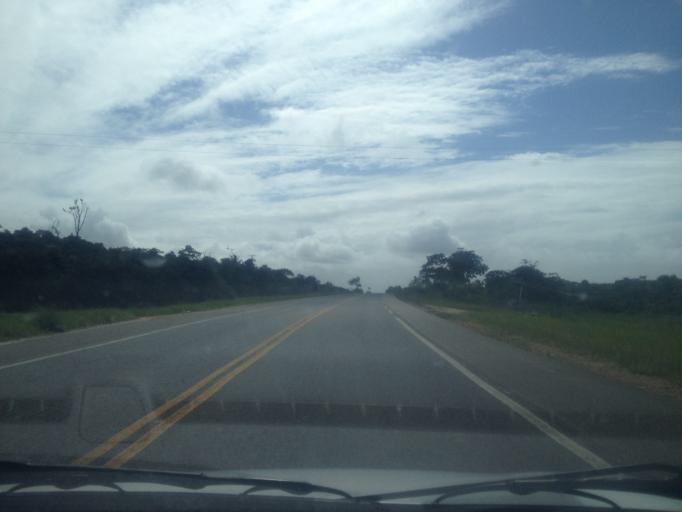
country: BR
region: Bahia
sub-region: Conde
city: Conde
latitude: -11.8453
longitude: -37.6353
